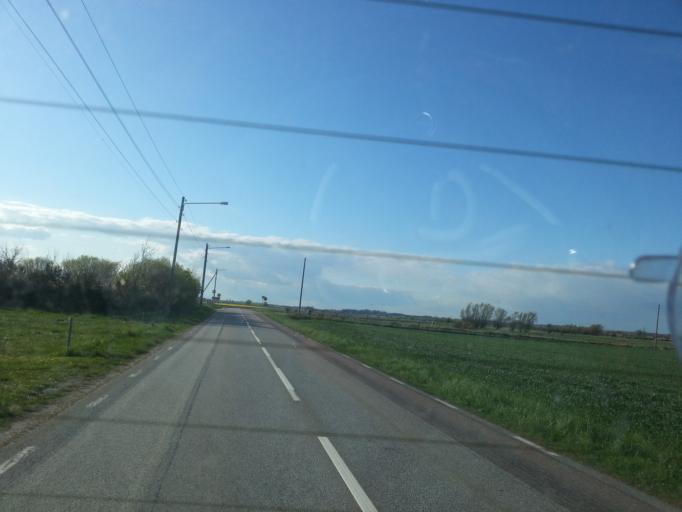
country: SE
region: Skane
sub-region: Ystads Kommun
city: Kopingebro
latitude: 55.4116
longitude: 14.0156
